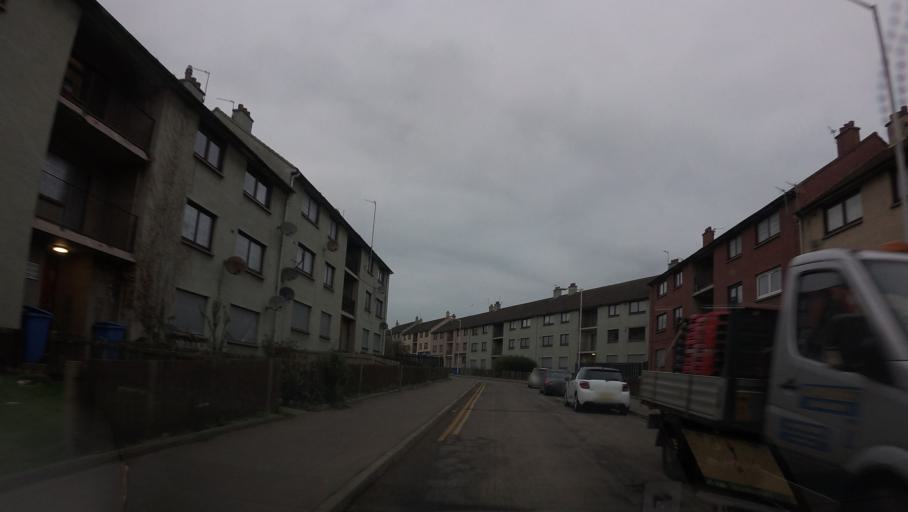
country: GB
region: Scotland
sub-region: Fife
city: Inverkeithing
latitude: 56.0299
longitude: -3.3885
